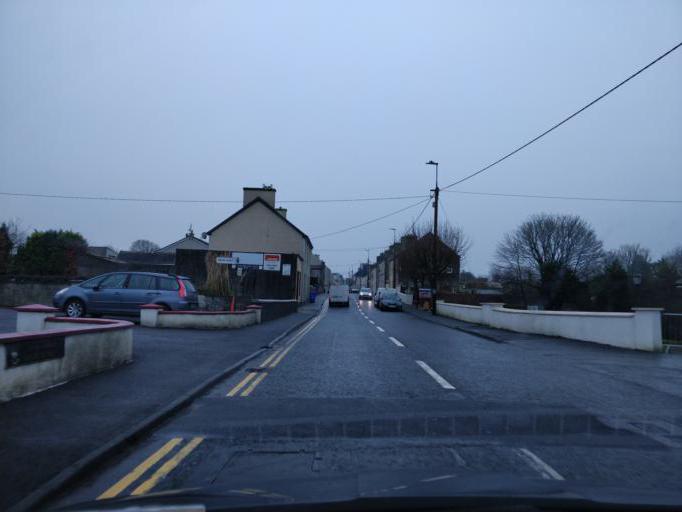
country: IE
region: Connaught
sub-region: Maigh Eo
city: Kiltamagh
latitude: 53.8534
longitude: -8.9957
